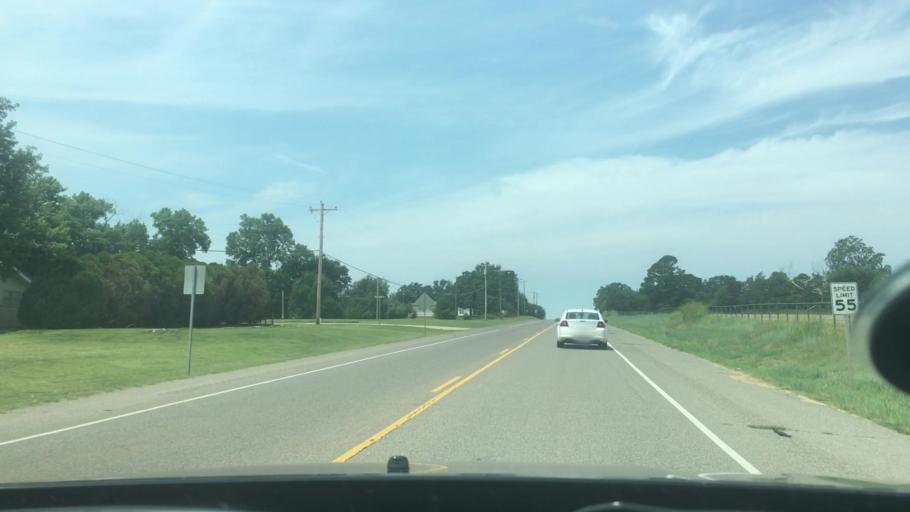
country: US
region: Oklahoma
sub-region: Pottawatomie County
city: Shawnee
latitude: 35.3332
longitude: -96.8469
